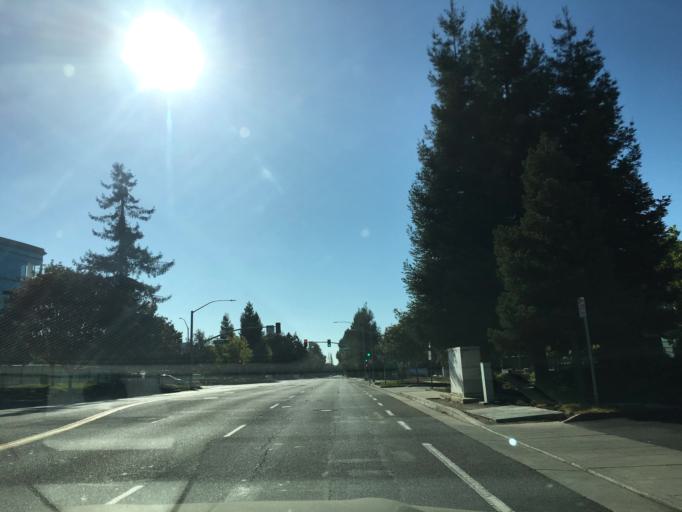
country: US
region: California
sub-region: Santa Clara County
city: Sunnyvale
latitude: 37.3932
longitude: -122.0409
